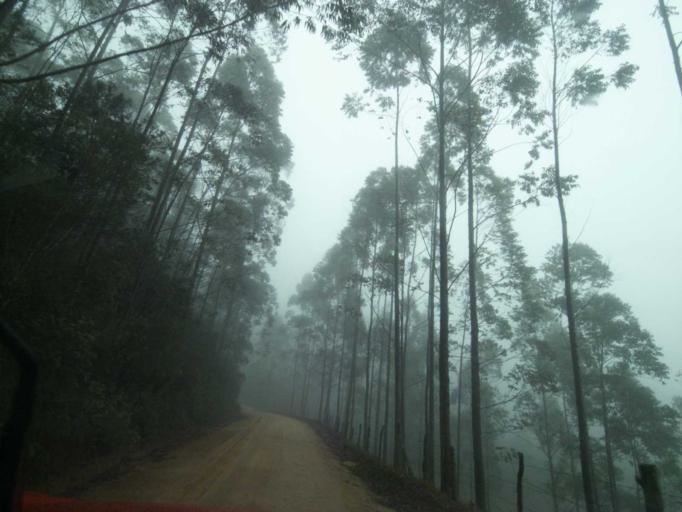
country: BR
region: Santa Catarina
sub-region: Anitapolis
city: Anitapolis
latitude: -27.9186
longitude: -49.1749
